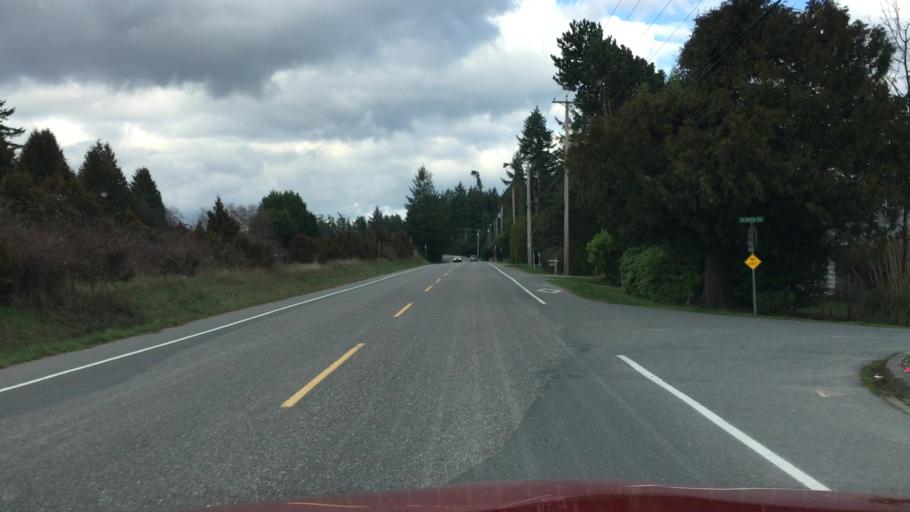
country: CA
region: British Columbia
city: North Saanich
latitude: 48.6026
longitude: -123.3961
